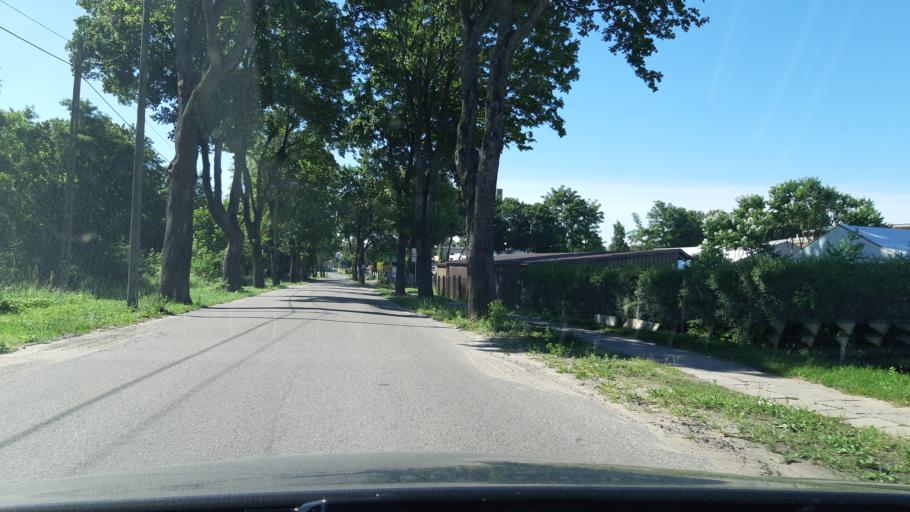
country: PL
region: Warmian-Masurian Voivodeship
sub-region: Powiat mragowski
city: Mragowo
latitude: 53.8579
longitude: 21.2955
